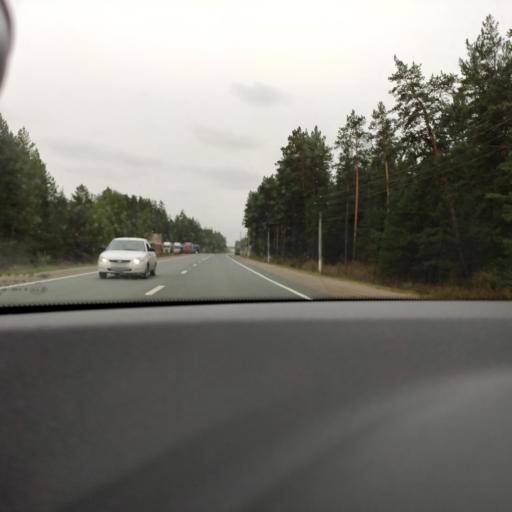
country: RU
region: Samara
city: Mirnyy
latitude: 53.5542
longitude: 50.2949
